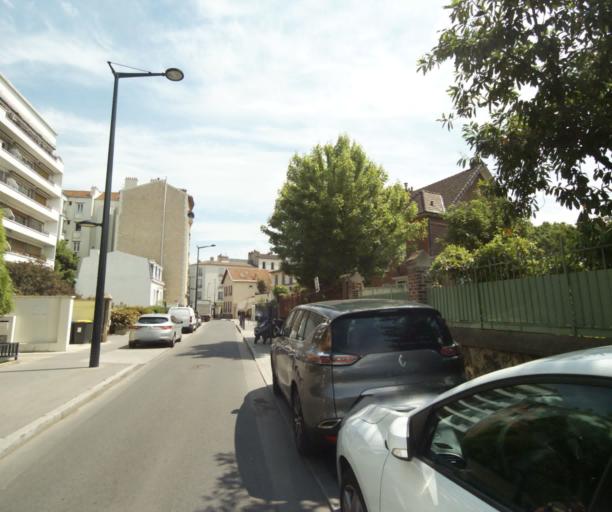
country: FR
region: Ile-de-France
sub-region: Departement des Hauts-de-Seine
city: Colombes
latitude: 48.9103
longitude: 2.2637
